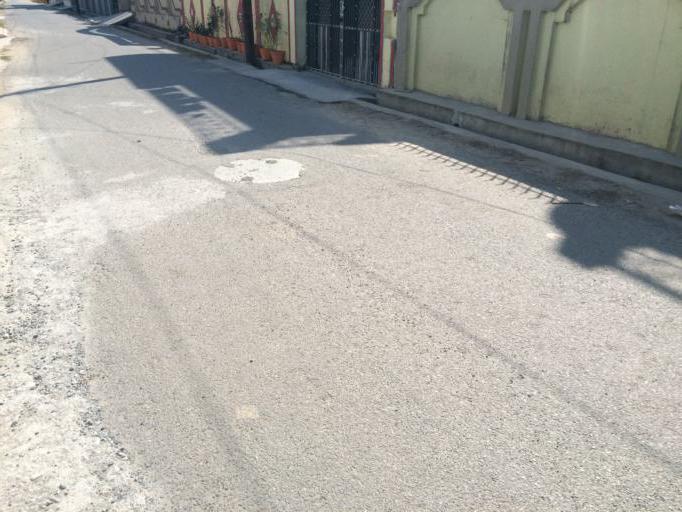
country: IN
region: Uttarakhand
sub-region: Dehradun
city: Dehradun
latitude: 30.2878
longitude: 78.0564
